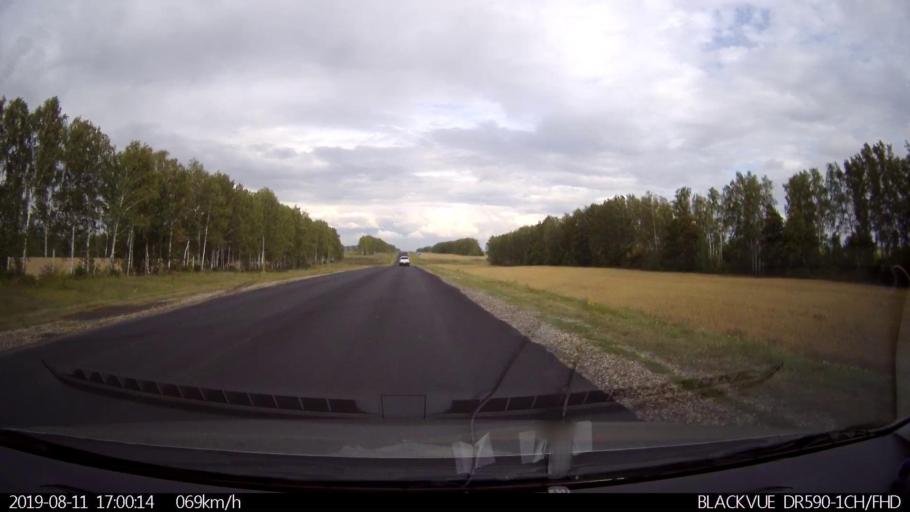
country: RU
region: Ulyanovsk
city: Mayna
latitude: 54.3108
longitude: 47.6758
